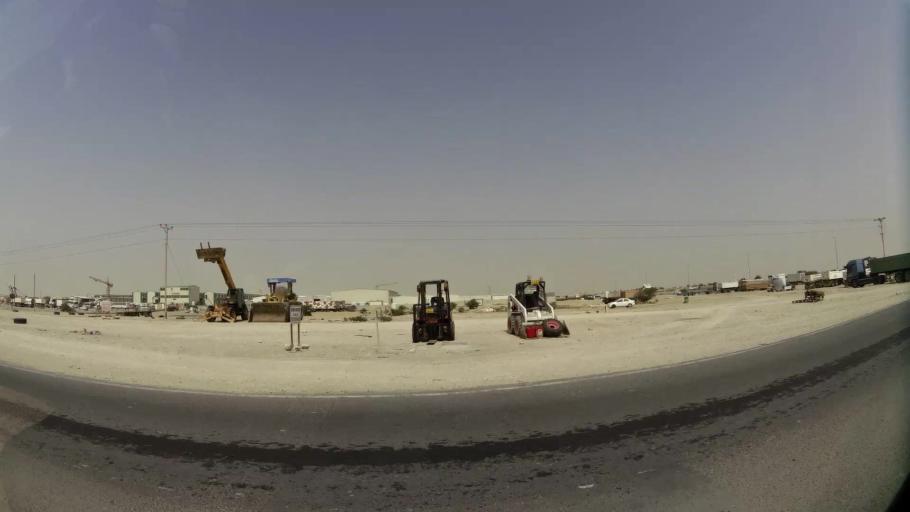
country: QA
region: Baladiyat ar Rayyan
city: Ar Rayyan
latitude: 25.2000
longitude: 51.3663
